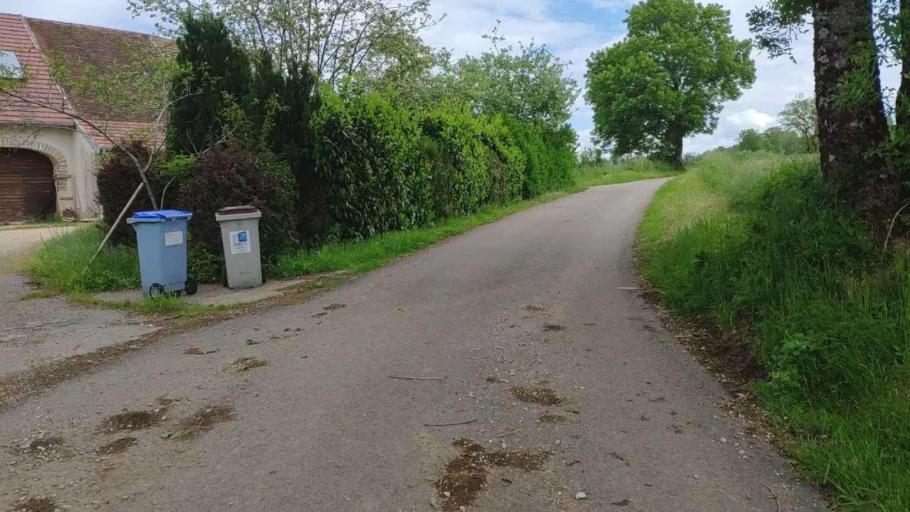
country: FR
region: Franche-Comte
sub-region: Departement du Jura
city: Poligny
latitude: 46.7669
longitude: 5.6556
